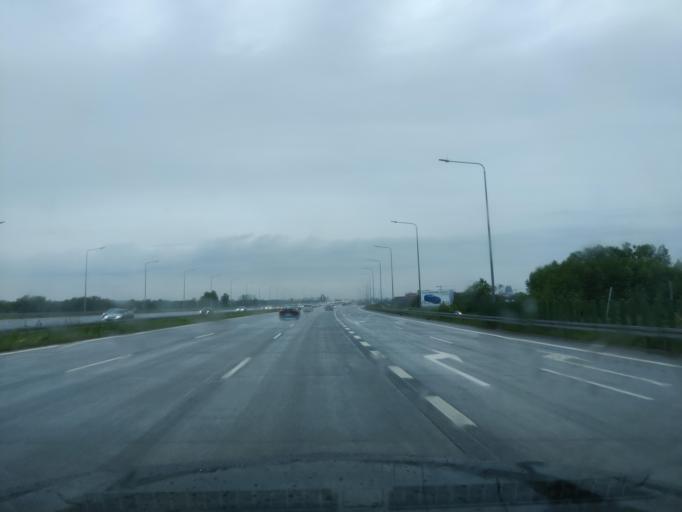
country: PL
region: Masovian Voivodeship
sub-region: Warszawa
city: Wilanow
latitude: 52.1504
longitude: 21.0999
